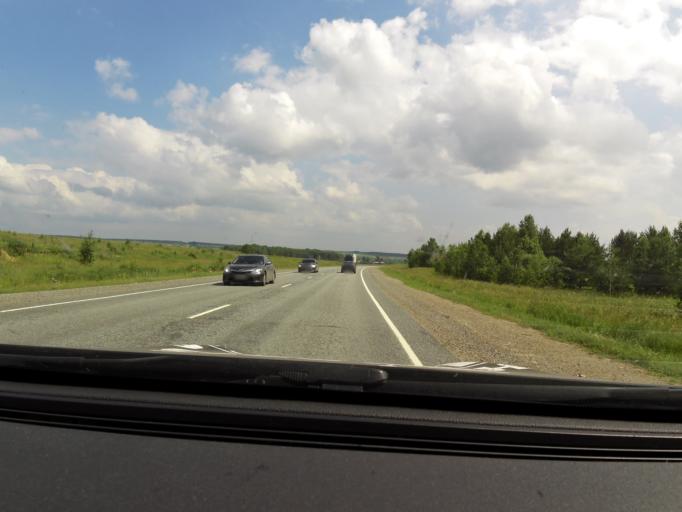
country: RU
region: Sverdlovsk
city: Achit
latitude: 56.7965
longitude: 57.8660
